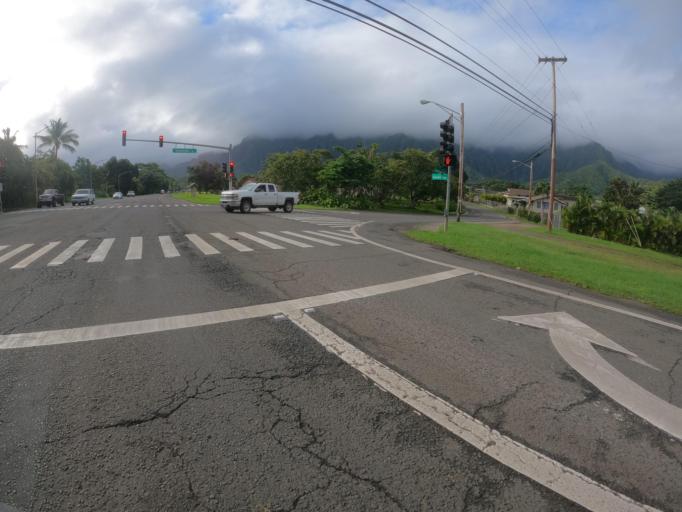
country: US
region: Hawaii
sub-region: Honolulu County
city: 'Ahuimanu
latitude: 21.4494
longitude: -157.8332
